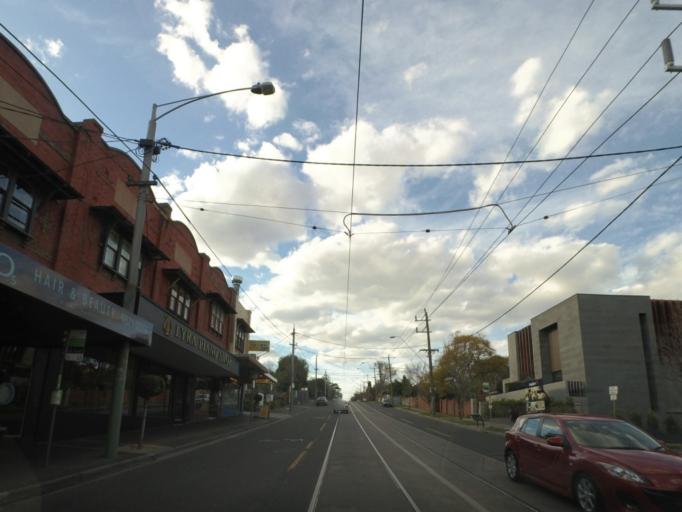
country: AU
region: Victoria
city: Glenferrie
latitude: -37.8438
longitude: 145.0543
